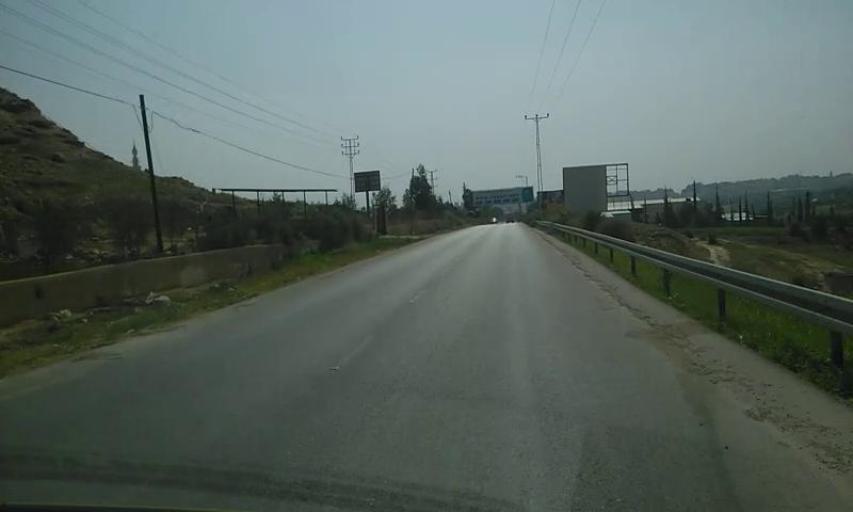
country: PS
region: West Bank
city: An Nuway`imah
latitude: 31.8905
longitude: 35.4315
